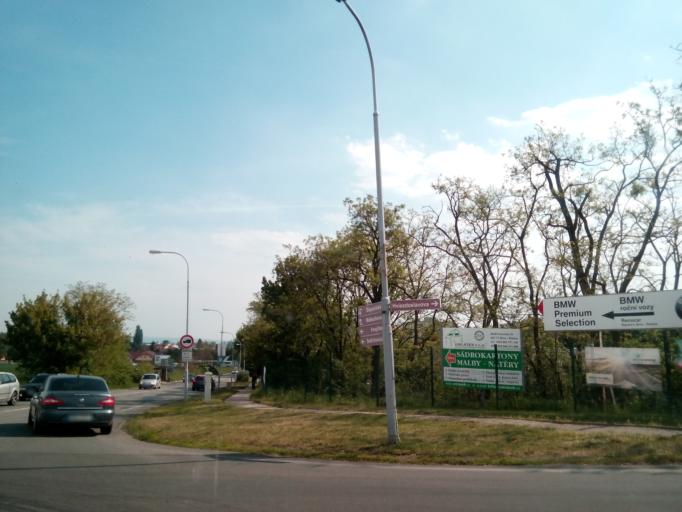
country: CZ
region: South Moravian
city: Podoli
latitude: 49.1823
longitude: 16.6918
